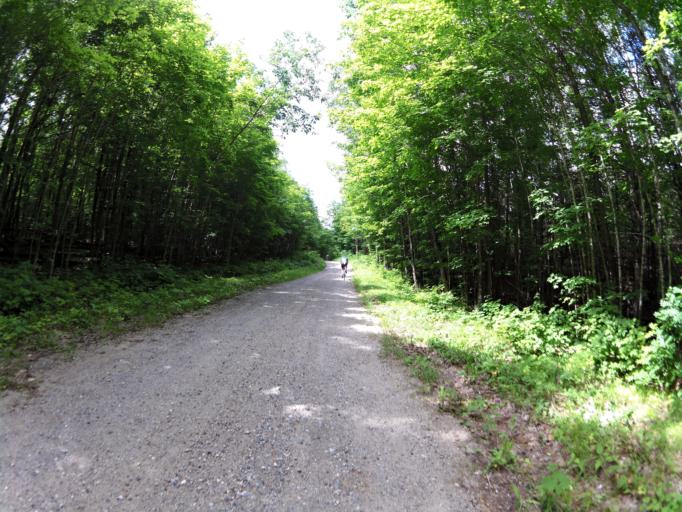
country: CA
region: Ontario
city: Perth
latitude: 45.0224
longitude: -76.5542
